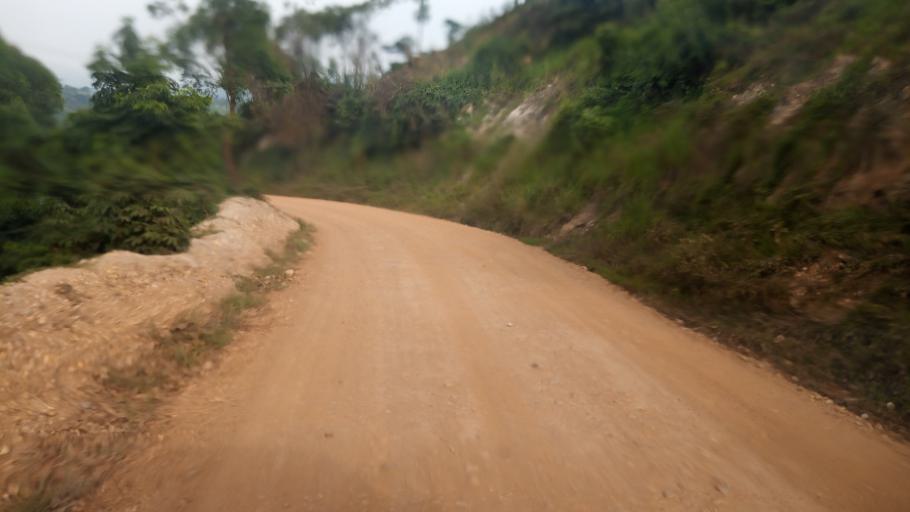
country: UG
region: Western Region
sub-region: Kanungu District
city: Ntungamo
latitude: -0.8388
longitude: 29.6470
